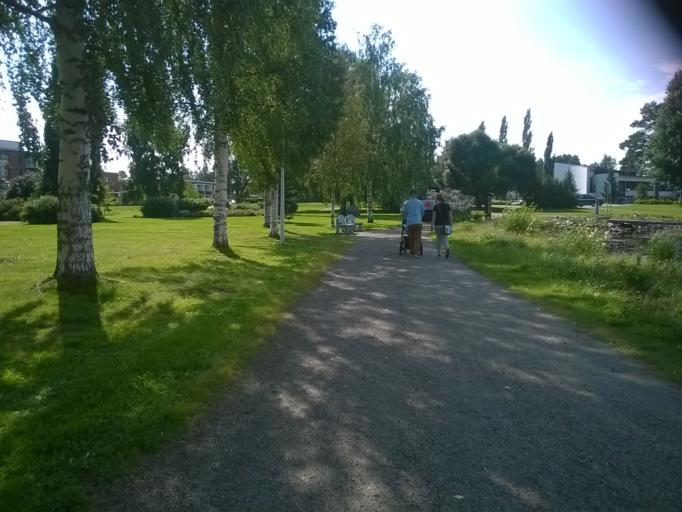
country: FI
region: Kainuu
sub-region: Kehys-Kainuu
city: Kuhmo
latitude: 64.1291
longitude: 29.5161
